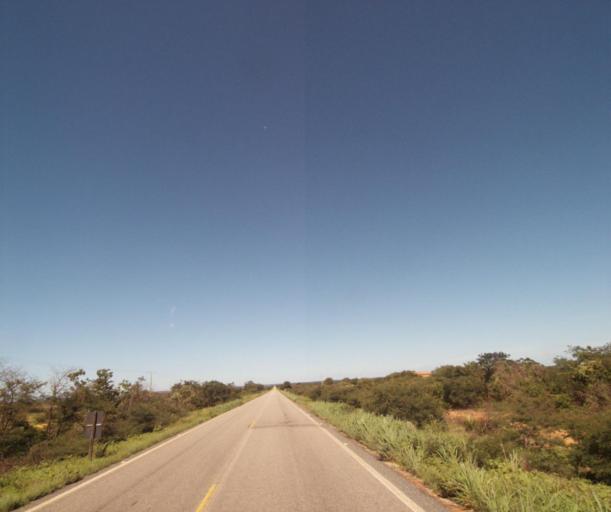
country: BR
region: Bahia
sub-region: Palmas De Monte Alto
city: Palmas de Monte Alto
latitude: -14.2560
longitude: -43.2425
